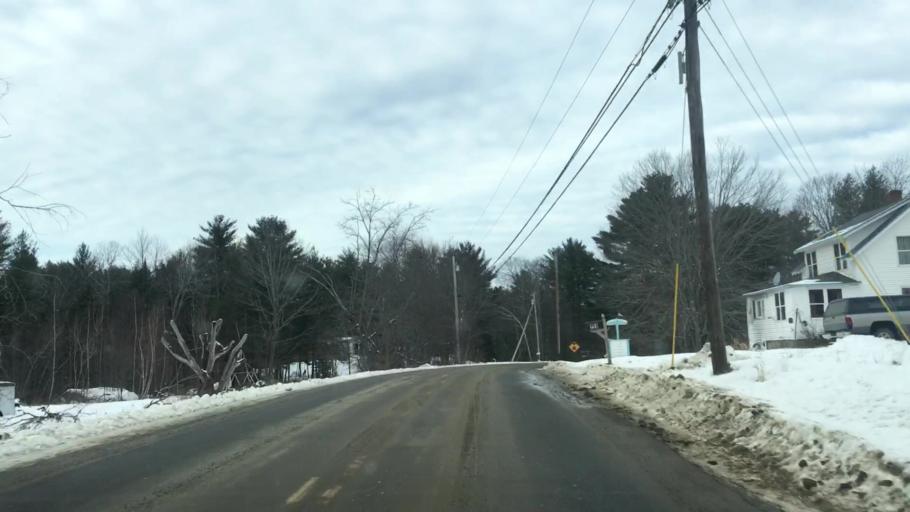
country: US
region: Maine
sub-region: Kennebec County
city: Chelsea
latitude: 44.2706
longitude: -69.6533
